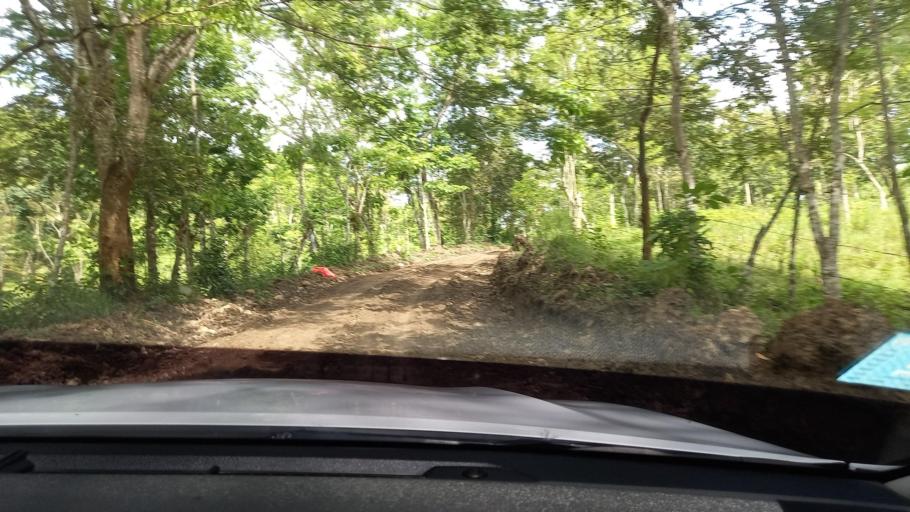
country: NI
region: Jinotega
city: San Jose de Bocay
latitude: 13.3820
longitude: -85.6861
